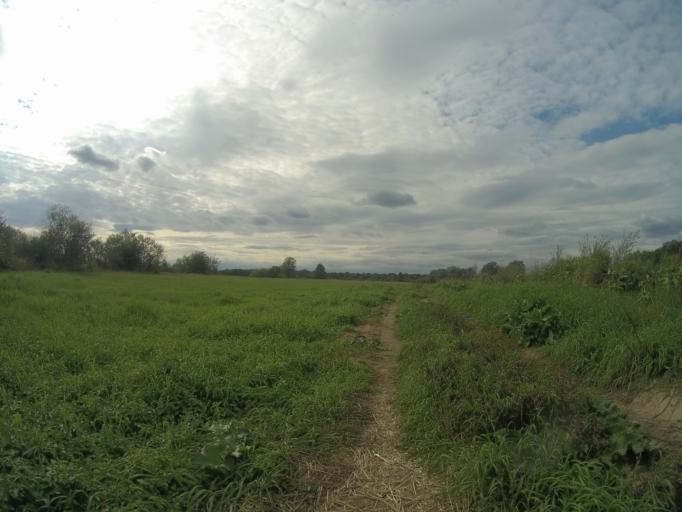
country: RU
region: Vladimir
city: Raduzhnyy
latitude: 56.0396
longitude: 40.2893
